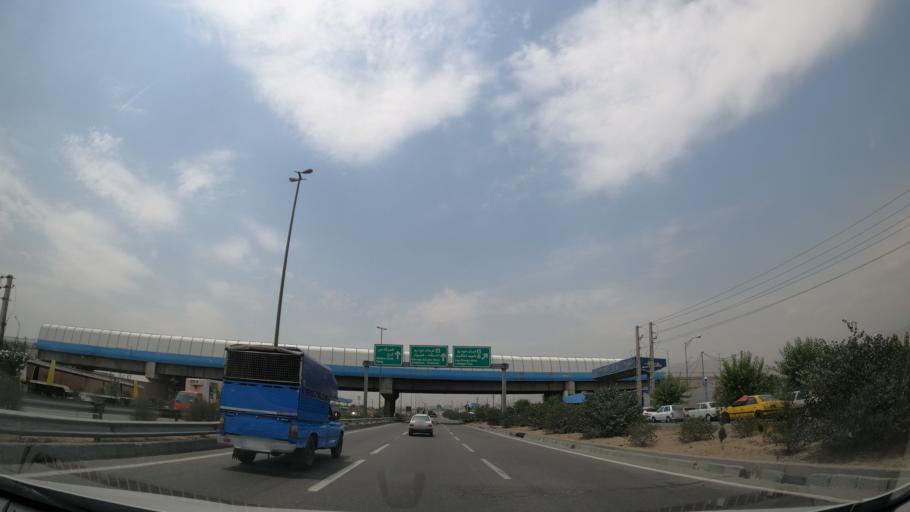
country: IR
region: Tehran
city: Shahr-e Qods
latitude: 35.7007
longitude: 51.1905
